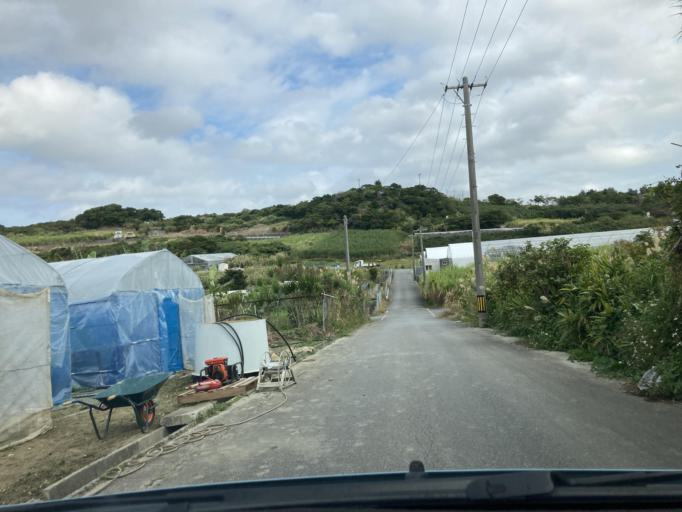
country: JP
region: Okinawa
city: Ginowan
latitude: 26.2106
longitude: 127.7433
